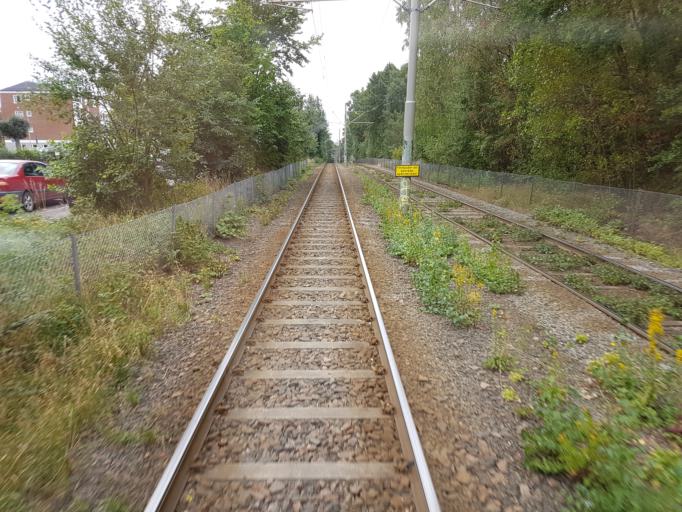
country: SE
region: Vaestra Goetaland
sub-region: Goteborg
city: Majorna
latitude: 57.6667
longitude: 11.9247
